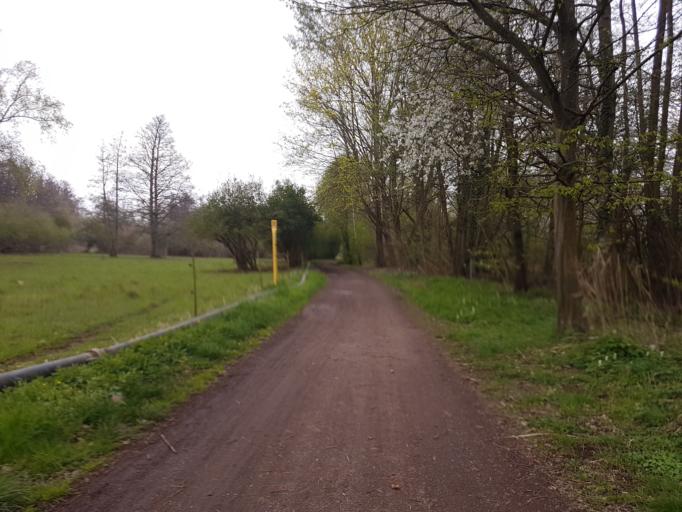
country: DE
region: Rheinland-Pfalz
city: Landau in der Pfalz
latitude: 49.2028
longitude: 8.0911
